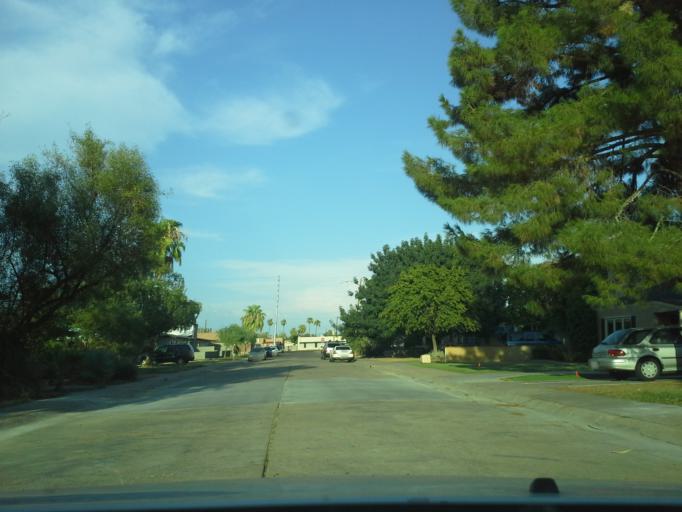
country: US
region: Arizona
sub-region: Maricopa County
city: Phoenix
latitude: 33.4725
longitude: -112.0671
